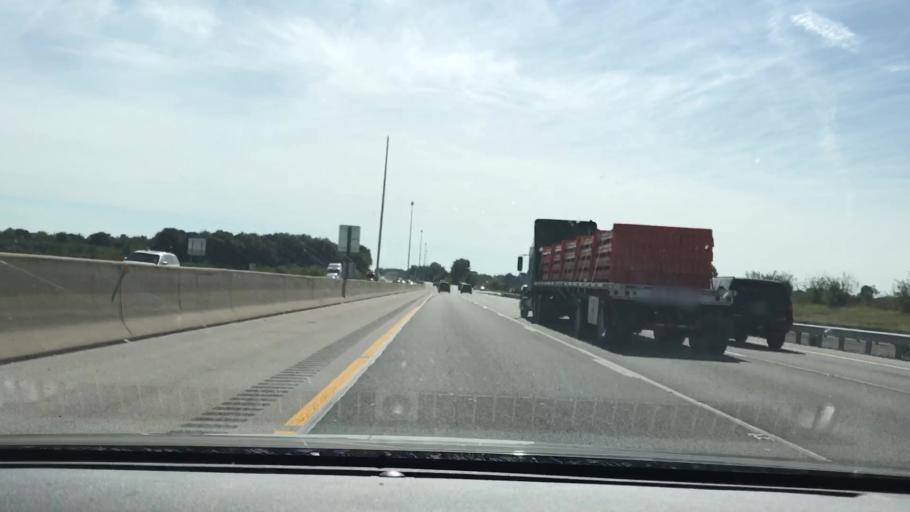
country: US
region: Kentucky
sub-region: Warren County
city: Plano
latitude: 36.9048
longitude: -86.4346
